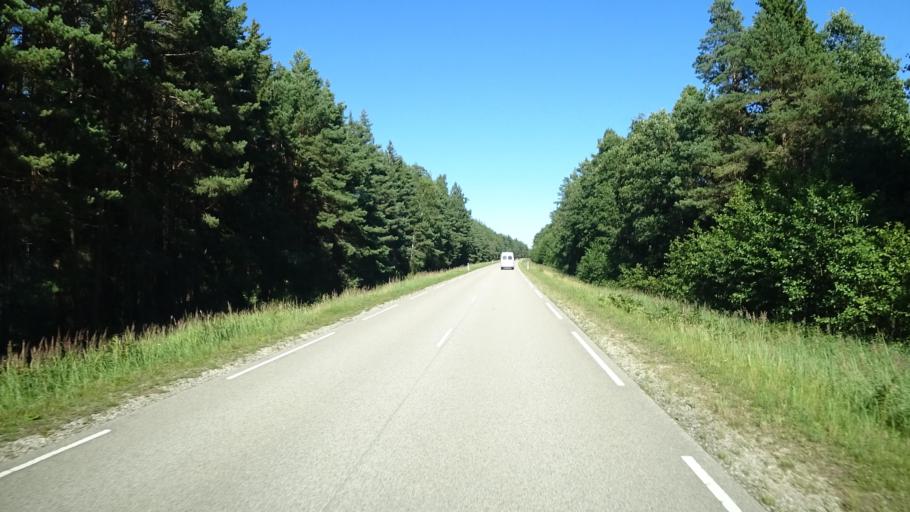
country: LV
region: Dundaga
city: Dundaga
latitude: 57.7420
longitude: 22.5458
